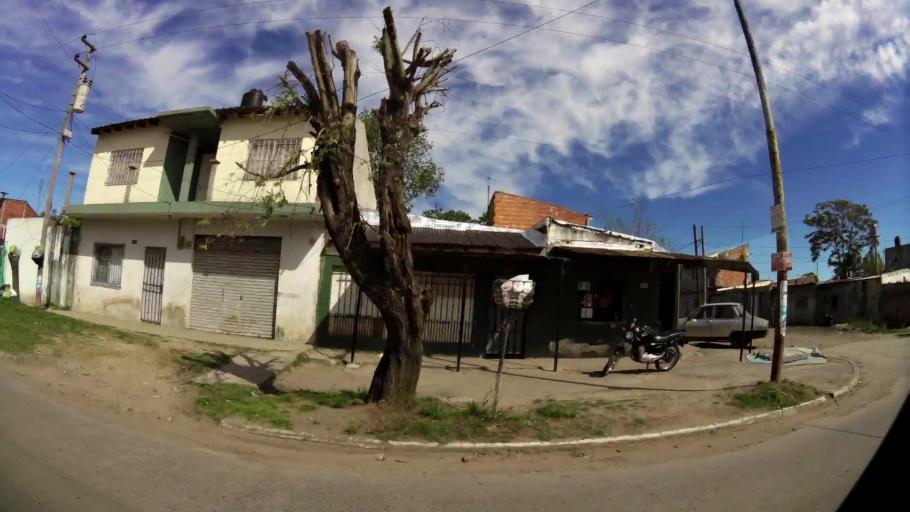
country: AR
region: Buenos Aires
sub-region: Partido de Quilmes
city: Quilmes
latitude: -34.7781
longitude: -58.2992
